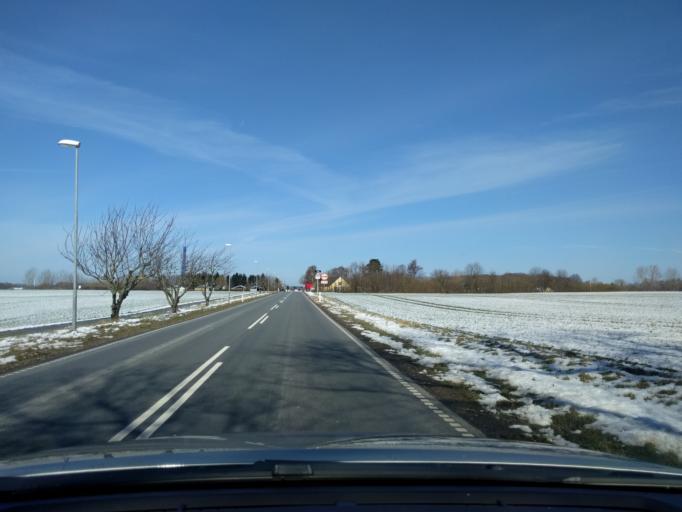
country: DK
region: South Denmark
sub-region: Nyborg Kommune
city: Ullerslev
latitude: 55.3600
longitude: 10.7282
